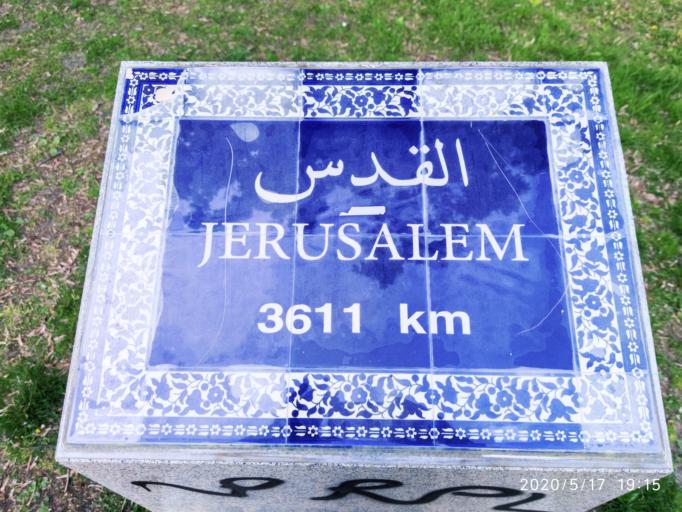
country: NO
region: Oslo
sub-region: Oslo
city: Oslo
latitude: 59.9235
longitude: 10.7460
